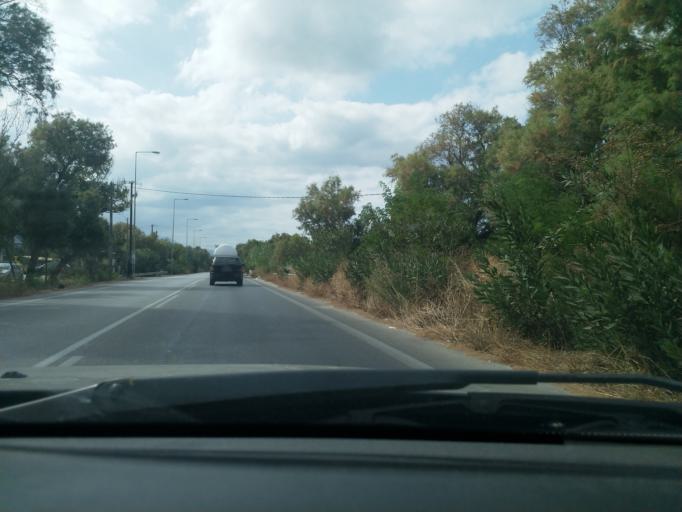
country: GR
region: Crete
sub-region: Nomos Chanias
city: Georgioupolis
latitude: 35.3529
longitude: 24.2870
